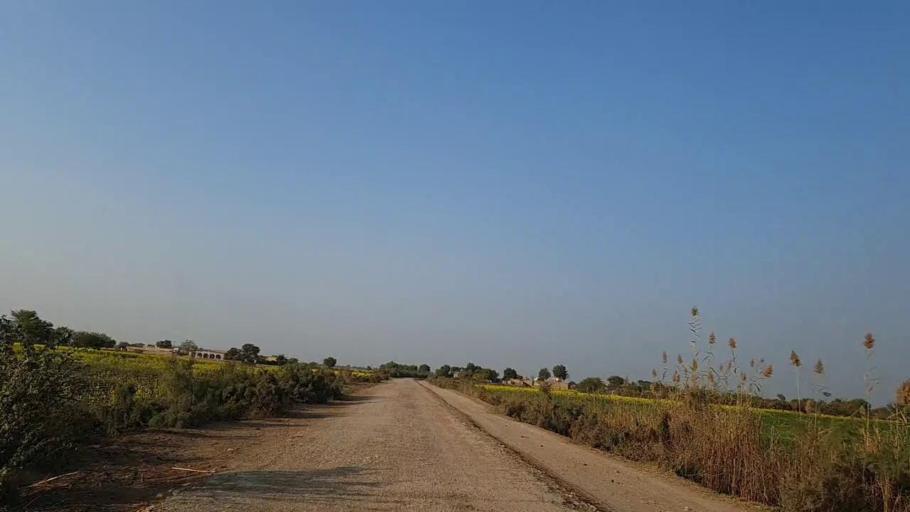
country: PK
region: Sindh
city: Sakrand
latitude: 26.1108
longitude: 68.3689
